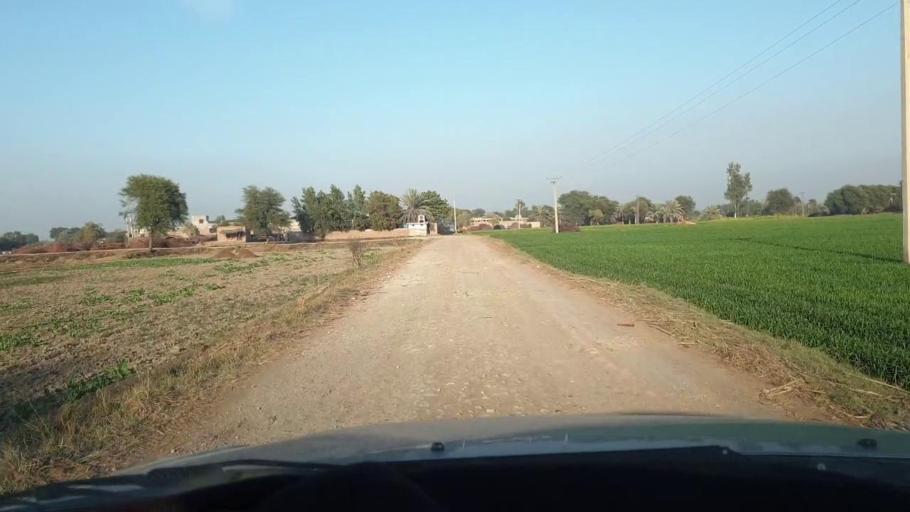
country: PK
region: Sindh
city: Mirpur Mathelo
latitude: 27.9847
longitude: 69.6292
